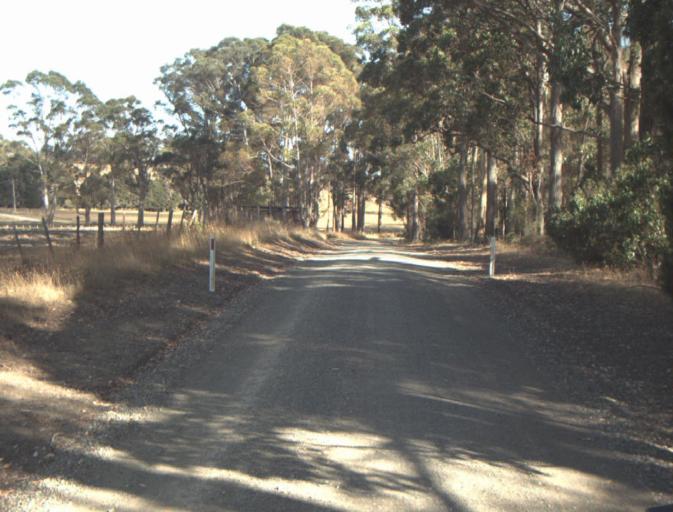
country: AU
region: Tasmania
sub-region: Dorset
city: Bridport
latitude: -41.1587
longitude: 147.2366
